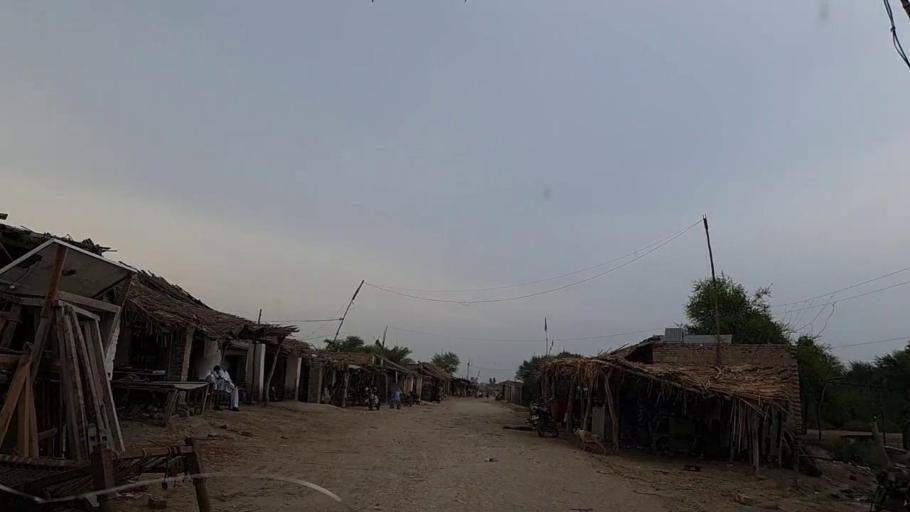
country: PK
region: Sindh
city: Mirpur Mathelo
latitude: 27.8969
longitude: 69.6559
